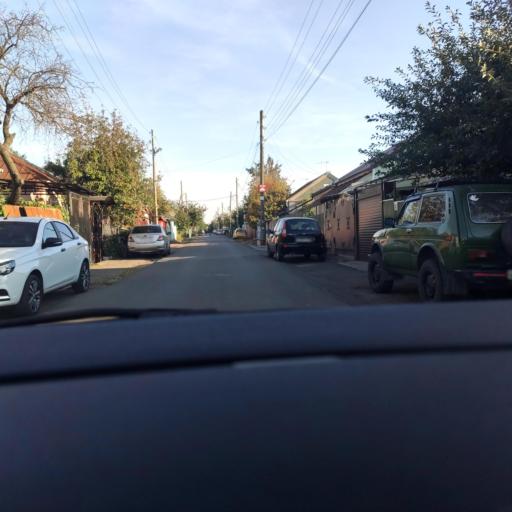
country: RU
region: Voronezj
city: Voronezh
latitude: 51.6293
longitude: 39.1685
